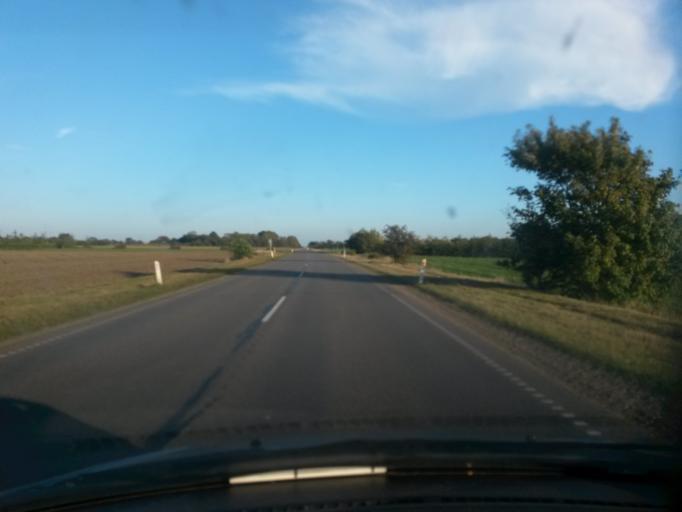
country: DK
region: Central Jutland
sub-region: Viborg Kommune
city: Karup
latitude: 56.3071
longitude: 9.2838
